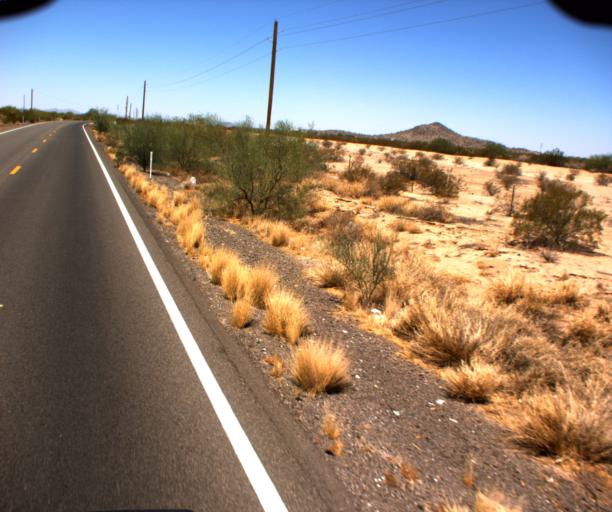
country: US
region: Arizona
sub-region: Pinal County
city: Maricopa
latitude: 33.0738
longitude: -112.1832
